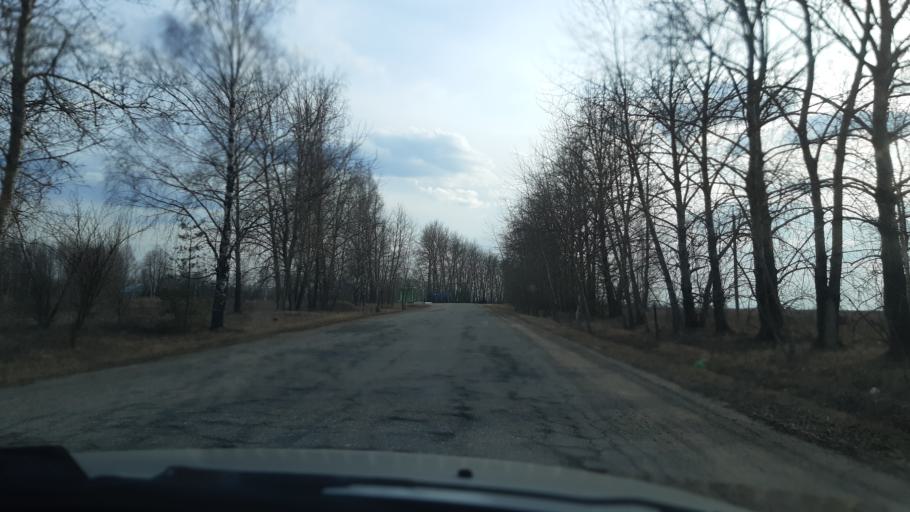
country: RU
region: Vladimir
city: Nikologory
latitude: 56.1062
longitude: 41.9807
